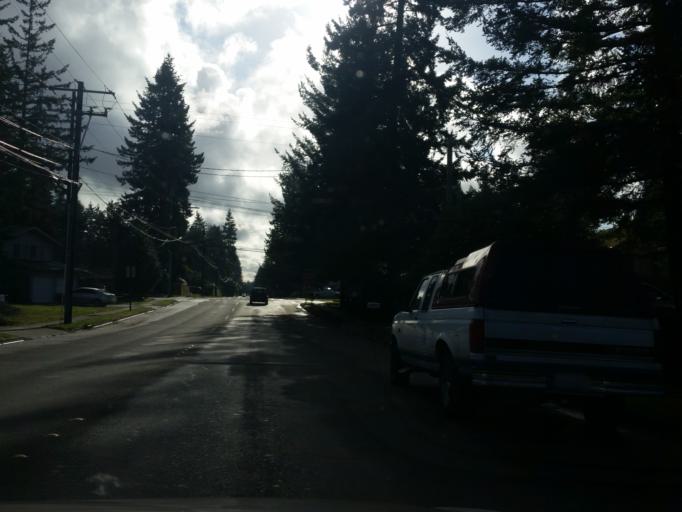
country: US
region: Washington
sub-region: Snohomish County
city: Lynnwood
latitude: 47.8294
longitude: -122.3197
